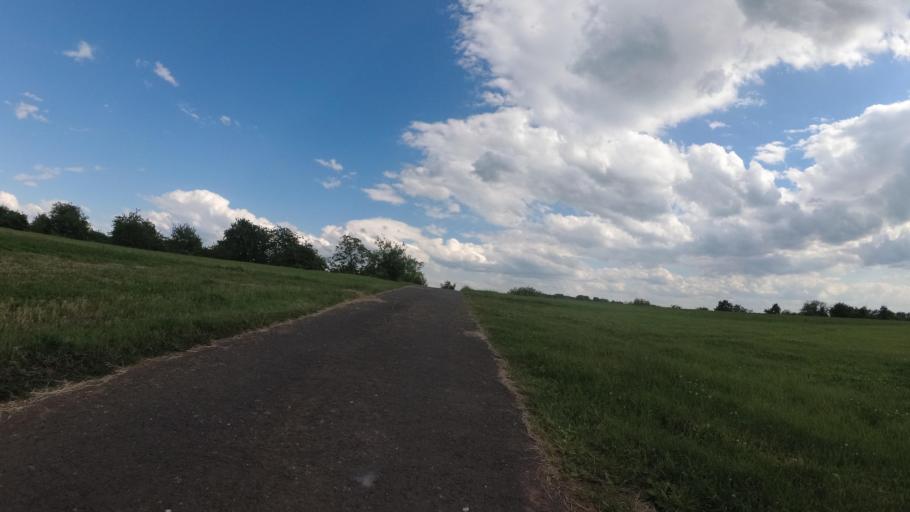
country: DE
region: Saarland
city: Namborn
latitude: 49.5134
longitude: 7.1699
